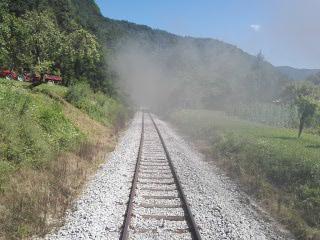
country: SI
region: Kanal
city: Kanal
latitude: 46.0947
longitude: 13.6379
